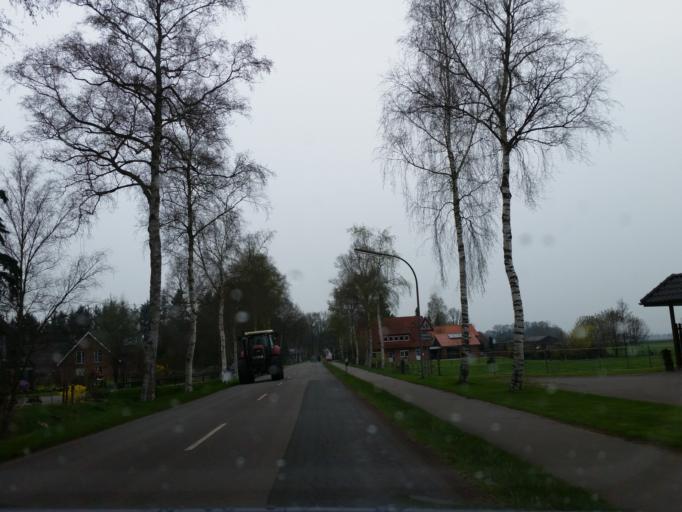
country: DE
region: Lower Saxony
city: Bei der Hohne
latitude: 53.5288
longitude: 9.1272
